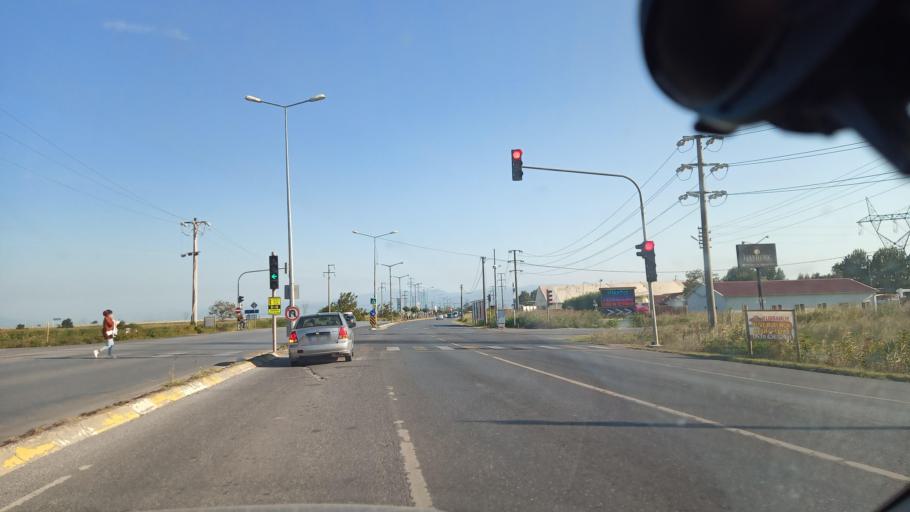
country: TR
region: Sakarya
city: Kazimpasa
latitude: 40.8360
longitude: 30.3457
